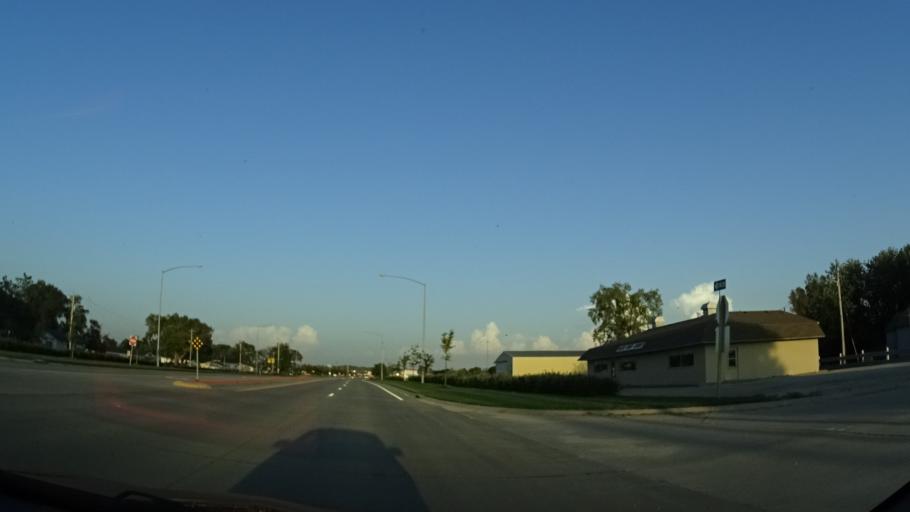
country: US
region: Iowa
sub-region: Pottawattamie County
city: Council Bluffs
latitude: 41.2196
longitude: -95.8586
